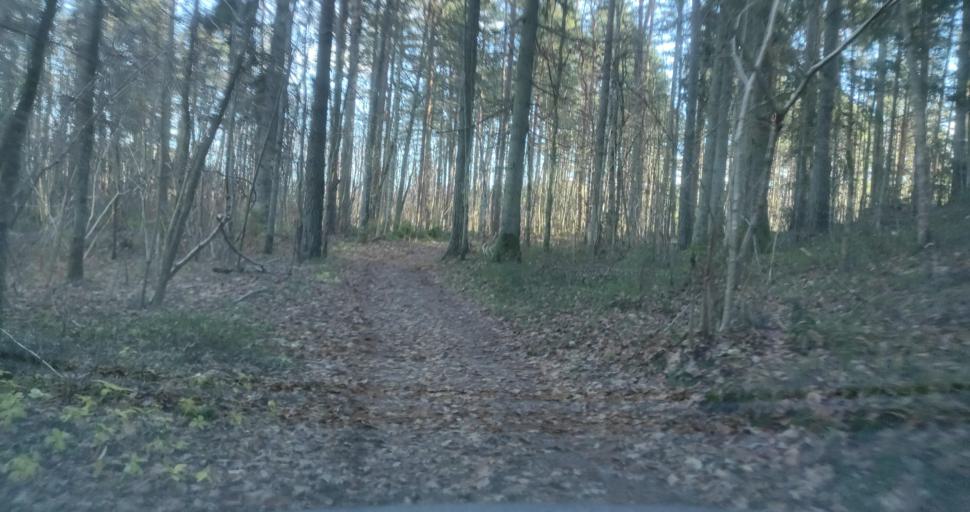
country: LV
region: Kuldigas Rajons
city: Kuldiga
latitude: 56.9613
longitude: 21.9297
